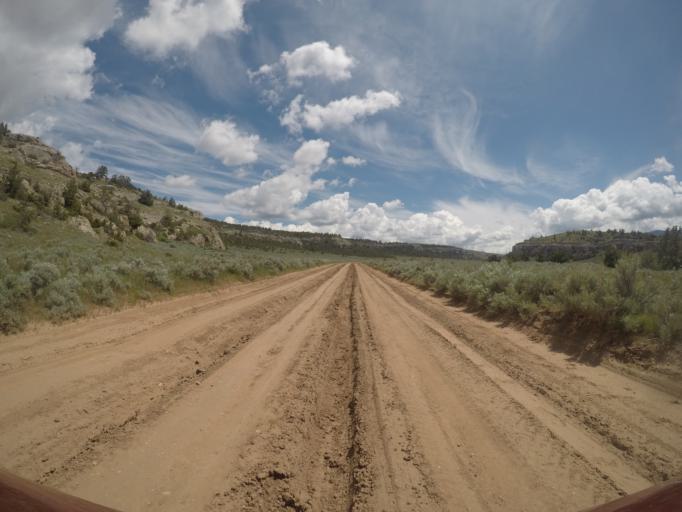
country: US
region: Montana
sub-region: Yellowstone County
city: Laurel
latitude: 45.2437
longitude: -108.6475
